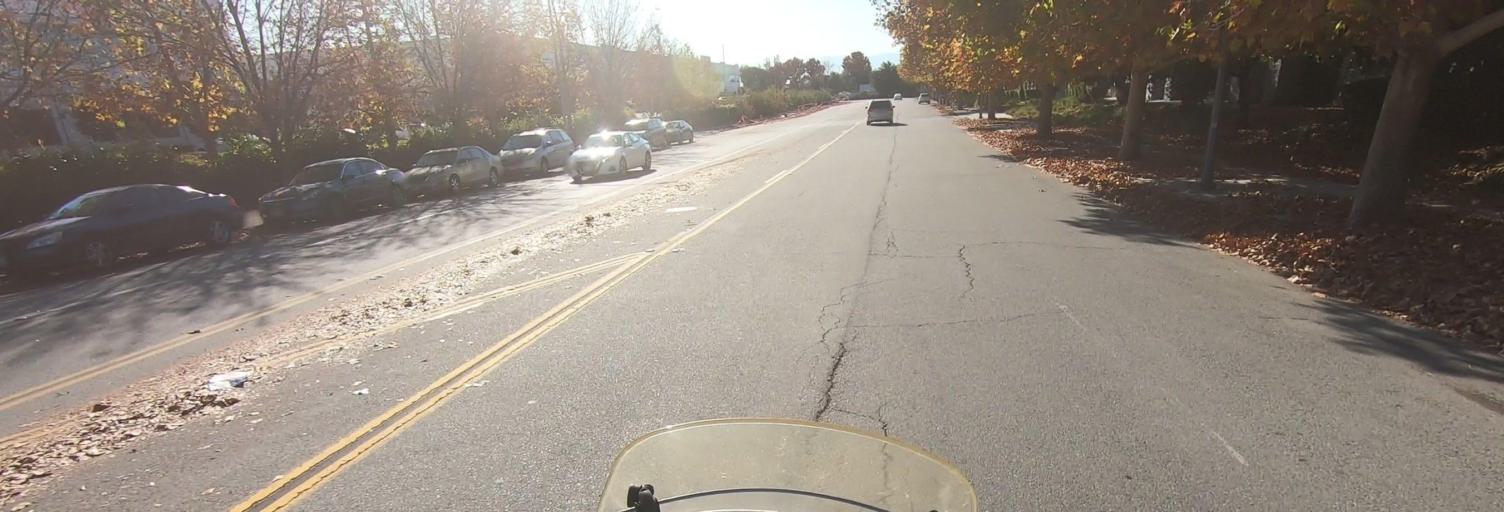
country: US
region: California
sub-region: Santa Clara County
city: San Jose
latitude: 37.3796
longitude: -121.9007
